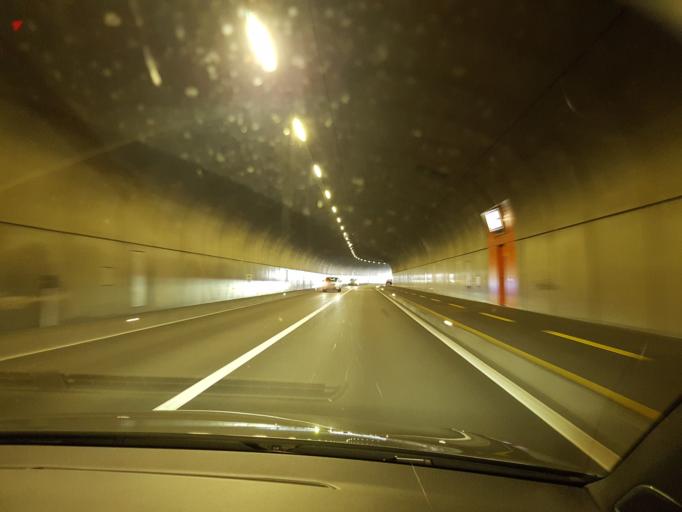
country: CH
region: Schwyz
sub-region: Bezirk Schwyz
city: Ingenbohl
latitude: 46.9709
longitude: 8.6119
